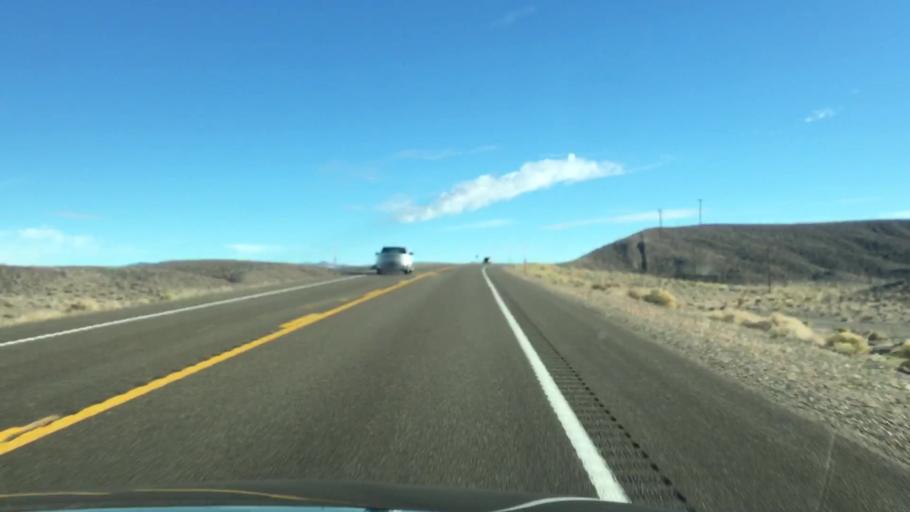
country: US
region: Nevada
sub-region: Mineral County
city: Hawthorne
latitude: 38.2198
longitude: -118.0085
